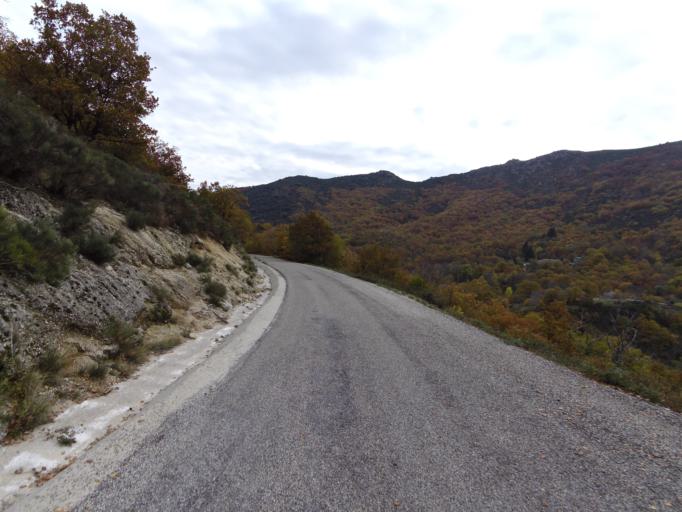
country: FR
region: Rhone-Alpes
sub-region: Departement de l'Ardeche
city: Les Vans
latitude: 44.4982
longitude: 4.0394
